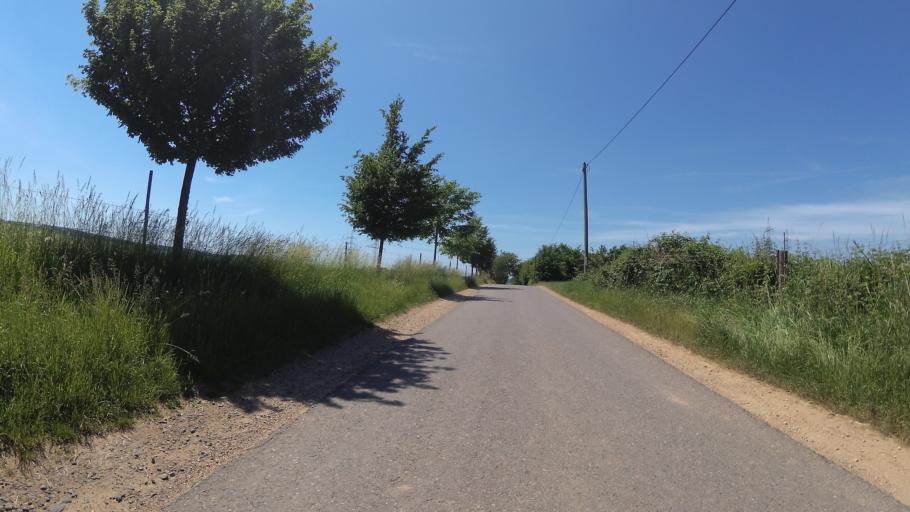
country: DE
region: Saarland
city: Eppelborn
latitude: 49.4022
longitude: 6.9431
